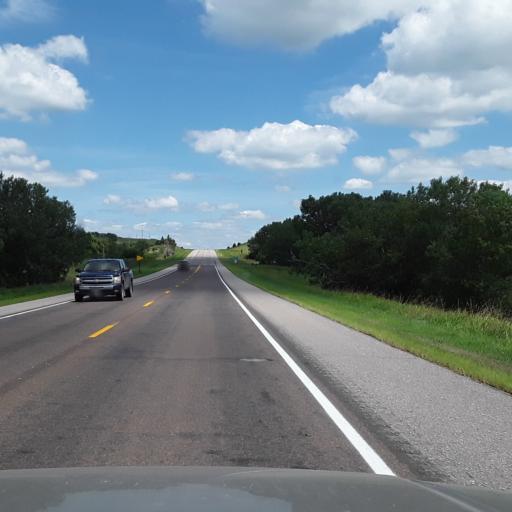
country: US
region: Nebraska
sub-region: Nance County
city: Genoa
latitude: 41.4711
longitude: -97.7070
